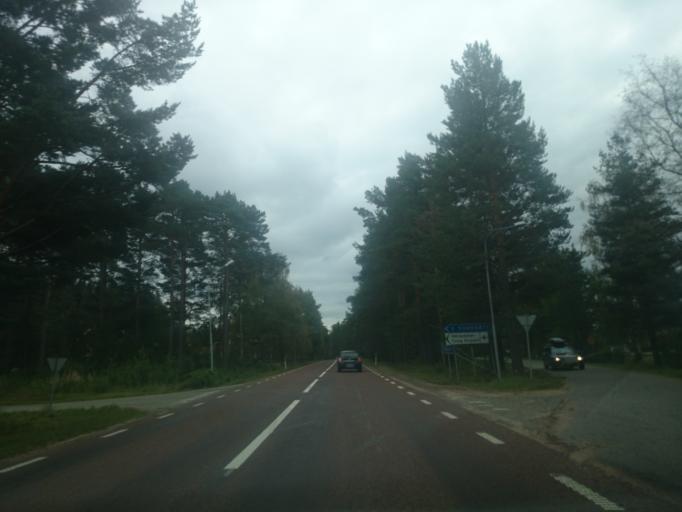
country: SE
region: Jaemtland
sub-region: Harjedalens Kommun
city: Sveg
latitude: 62.0378
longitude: 14.4073
